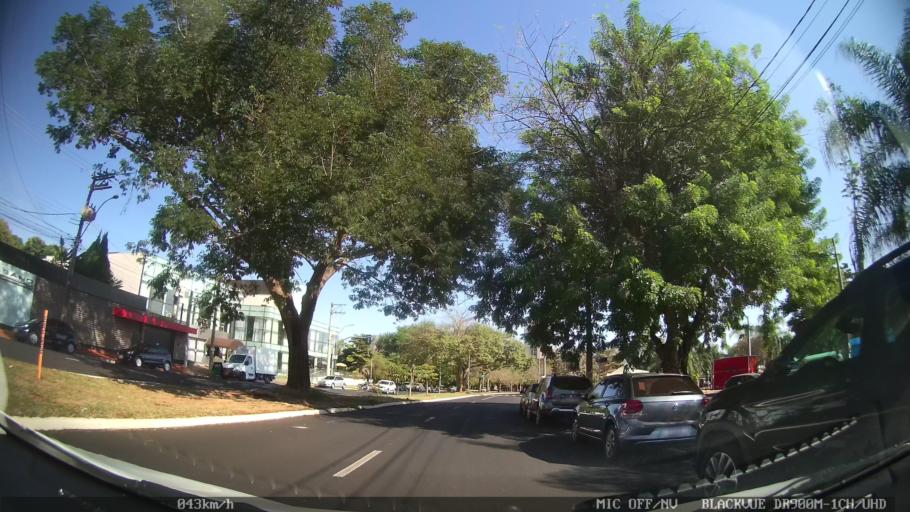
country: BR
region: Sao Paulo
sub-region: Ribeirao Preto
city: Ribeirao Preto
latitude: -21.2120
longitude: -47.8083
